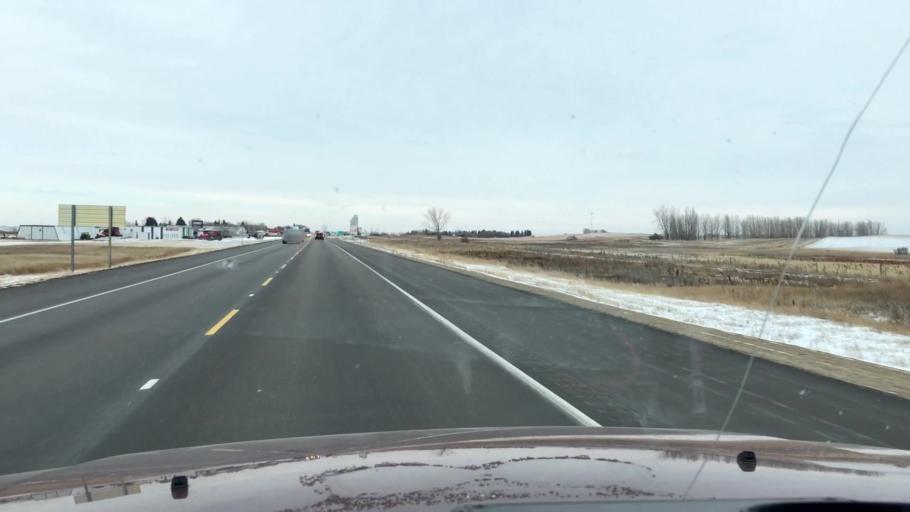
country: CA
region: Saskatchewan
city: Moose Jaw
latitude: 50.8571
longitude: -105.5802
